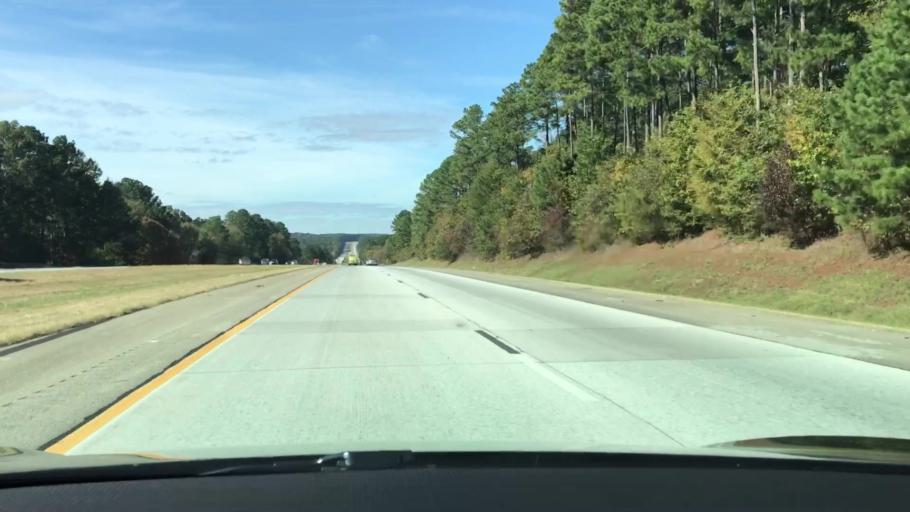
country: US
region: Georgia
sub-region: Greene County
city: Greensboro
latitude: 33.5355
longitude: -83.2544
